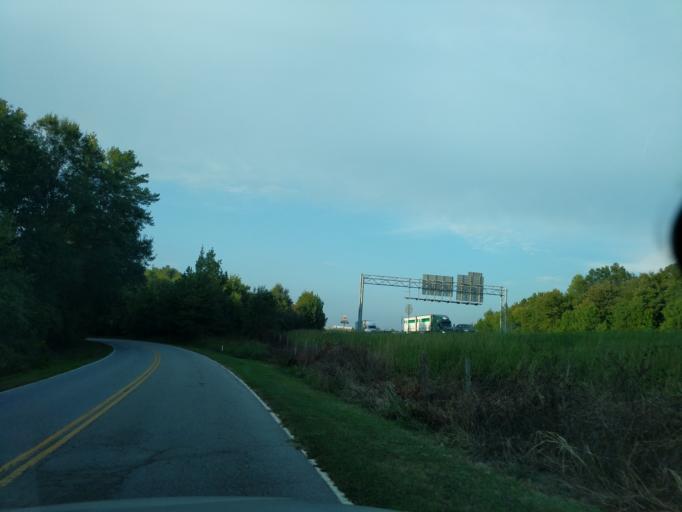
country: US
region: South Carolina
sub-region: Anderson County
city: Piedmont
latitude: 34.7050
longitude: -82.5013
